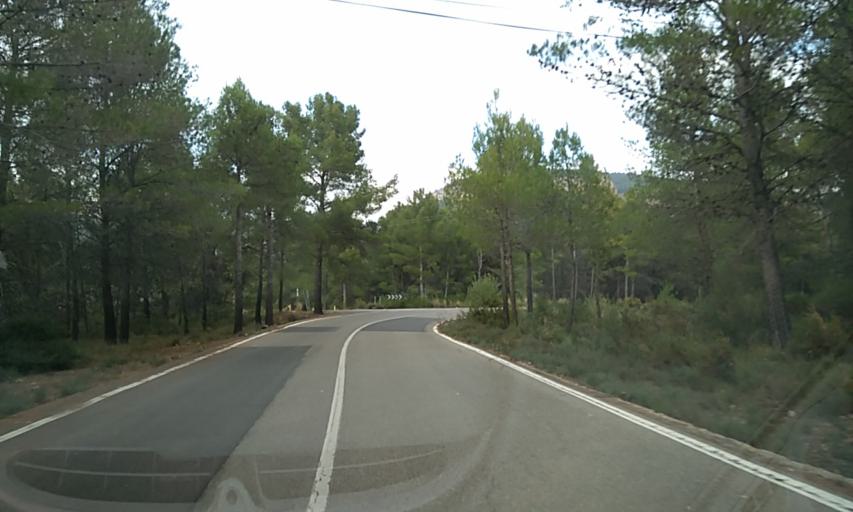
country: ES
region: Valencia
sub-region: Provincia de Castello
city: Puebla de Arenoso
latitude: 40.0877
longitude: -0.5622
